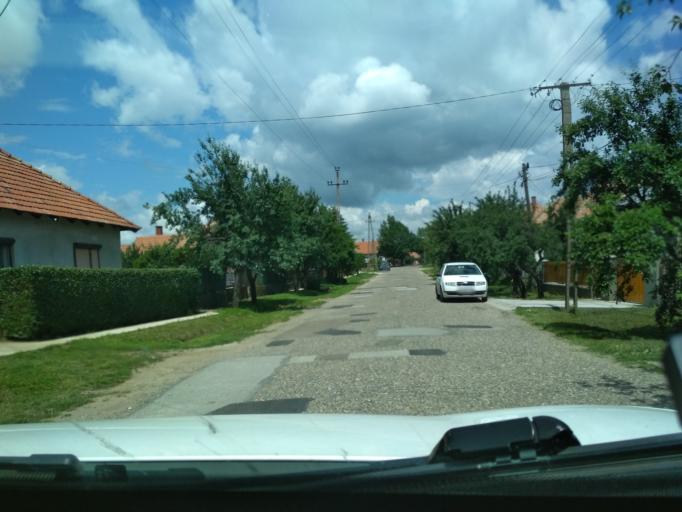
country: HU
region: Jasz-Nagykun-Szolnok
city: Tiszafured
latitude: 47.6118
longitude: 20.7714
